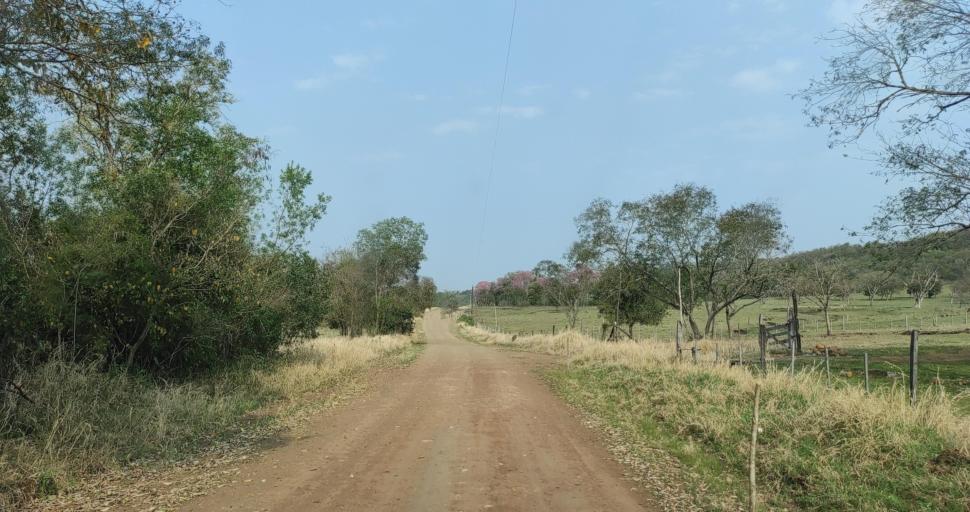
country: AR
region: Misiones
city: Cerro Azul
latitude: -27.6149
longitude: -55.5646
